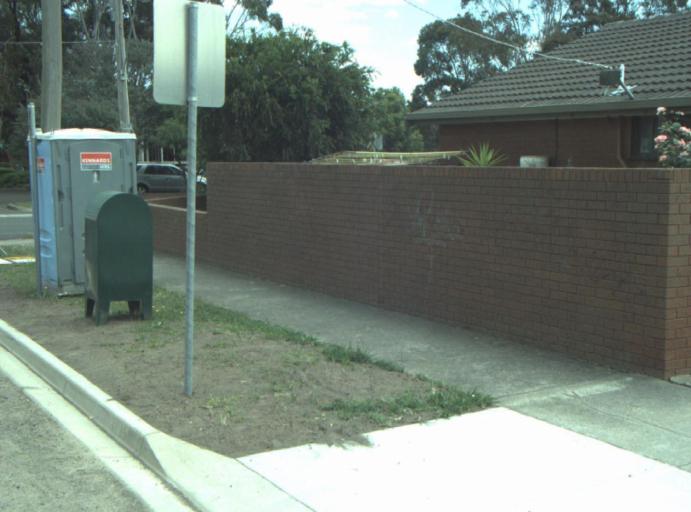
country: AU
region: Victoria
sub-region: Greater Geelong
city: Wandana Heights
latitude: -38.1849
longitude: 144.3260
